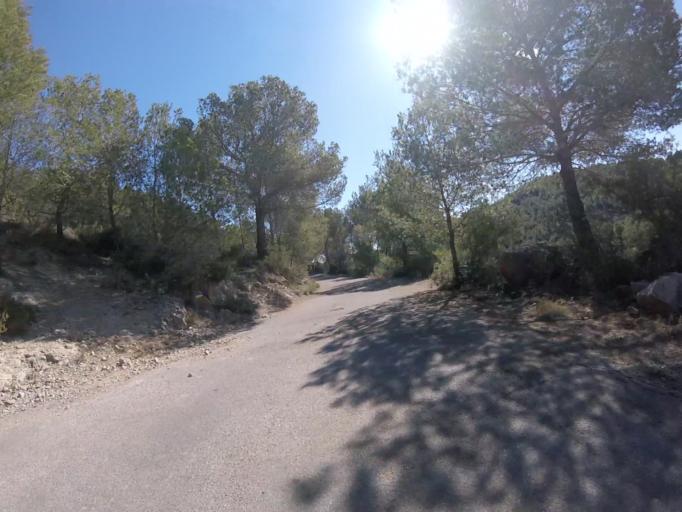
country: ES
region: Valencia
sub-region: Provincia de Castello
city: Benicassim
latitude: 40.0783
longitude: 0.0913
